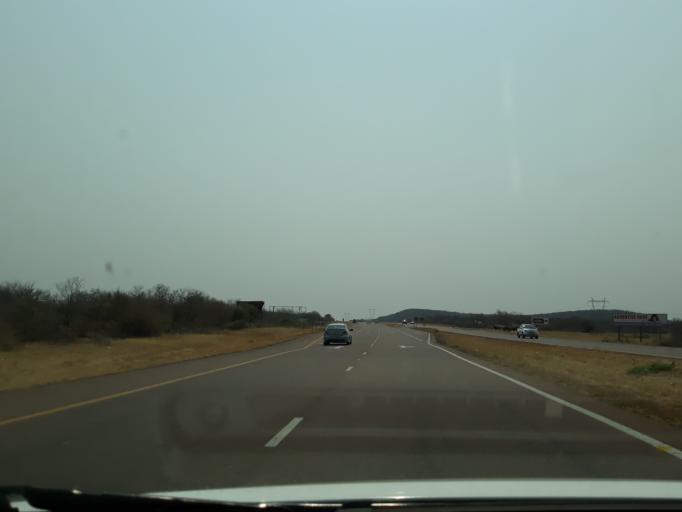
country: BW
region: Kgatleng
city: Bokaa
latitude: -24.4043
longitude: 26.0550
